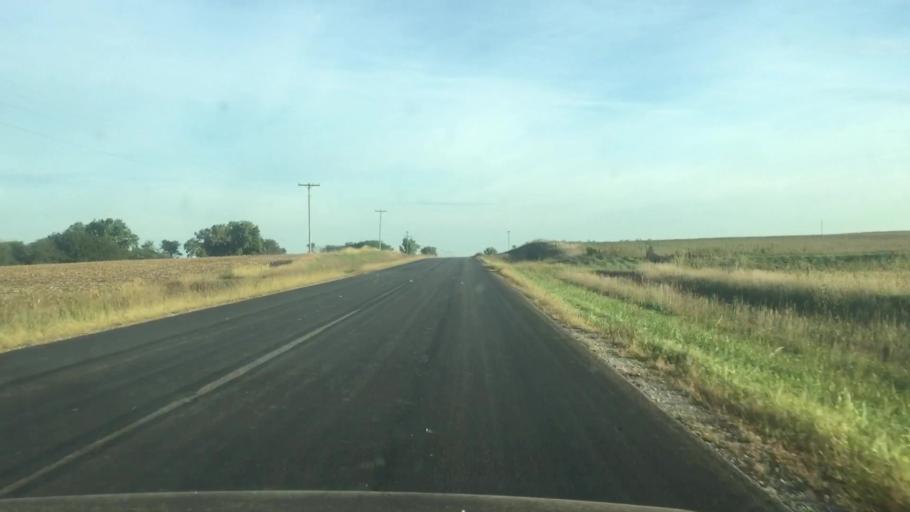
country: US
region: Kansas
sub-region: Marshall County
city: Marysville
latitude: 39.8777
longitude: -96.6009
